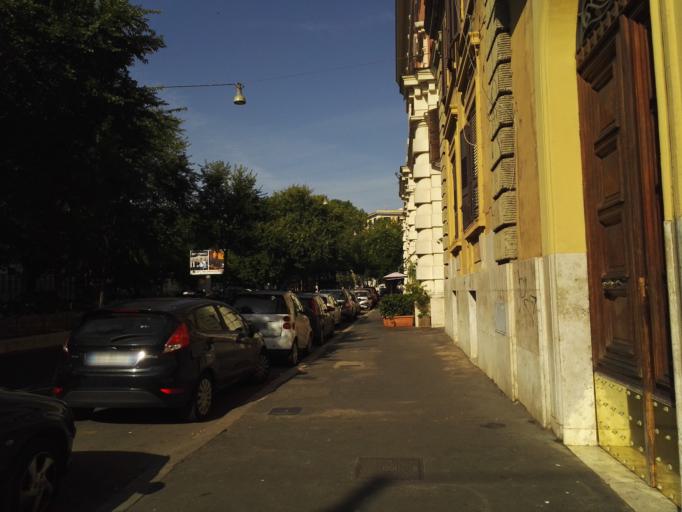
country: IT
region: Latium
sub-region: Citta metropolitana di Roma Capitale
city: Rome
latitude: 41.9035
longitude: 12.5086
